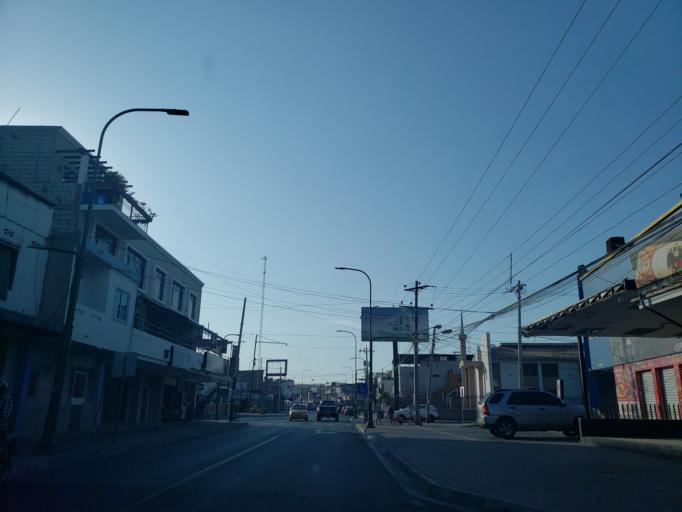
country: EC
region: Manabi
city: Manta
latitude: -0.9452
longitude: -80.7305
